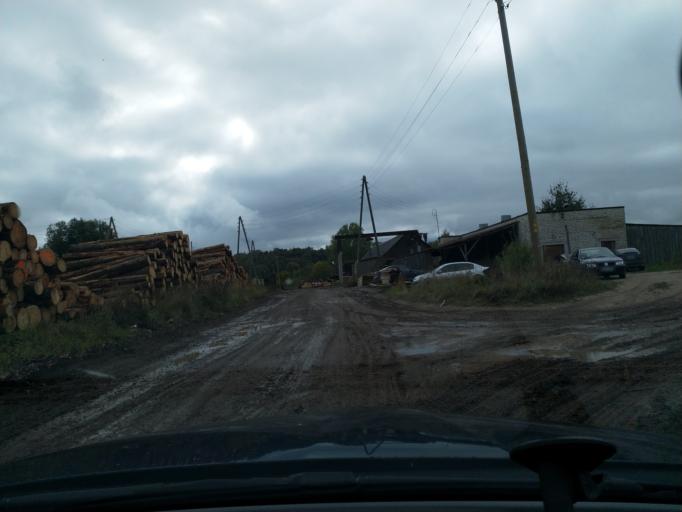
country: LV
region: Alsunga
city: Alsunga
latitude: 57.0258
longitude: 21.6738
